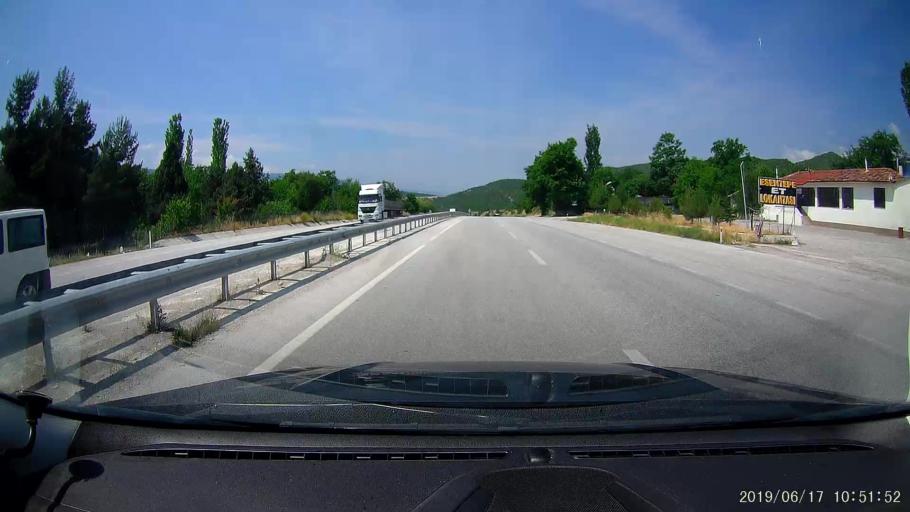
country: TR
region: Corum
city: Hacihamza
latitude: 41.0958
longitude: 34.3528
